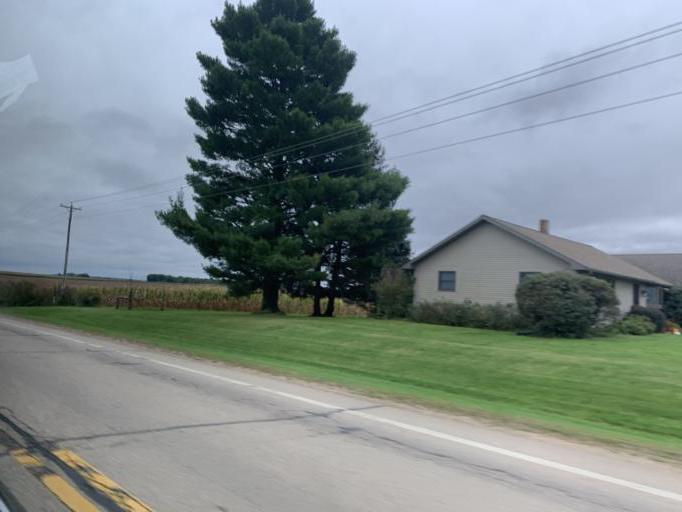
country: US
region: Wisconsin
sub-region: Grant County
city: Muscoda
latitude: 43.2198
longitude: -90.5021
